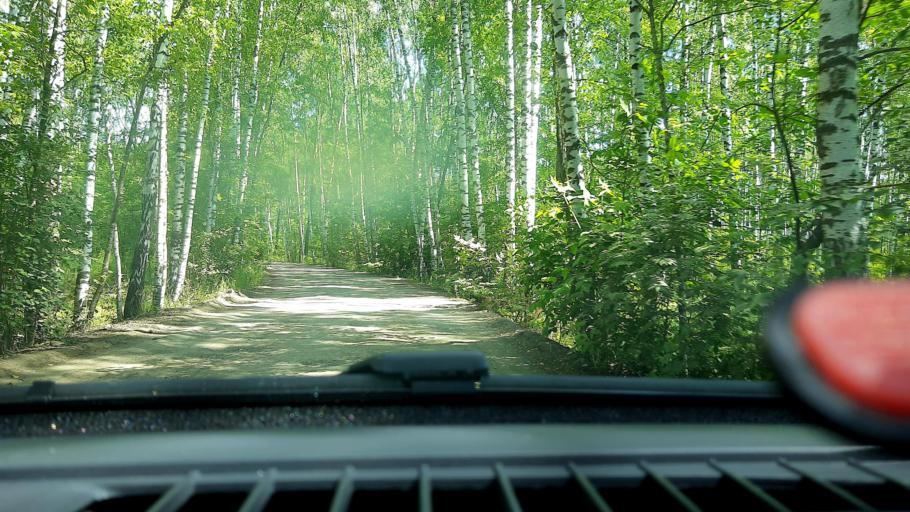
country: RU
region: Nizjnij Novgorod
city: Gorbatovka
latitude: 56.2967
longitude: 43.8186
